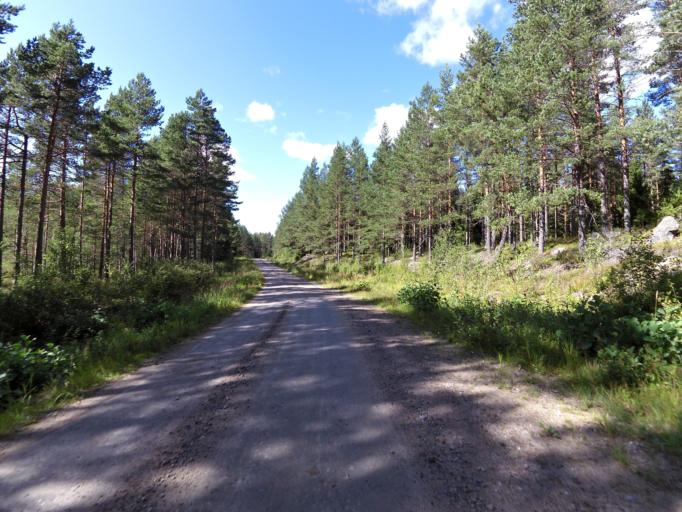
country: SE
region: Gaevleborg
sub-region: Ockelbo Kommun
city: Ockelbo
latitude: 60.7962
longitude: 16.8149
